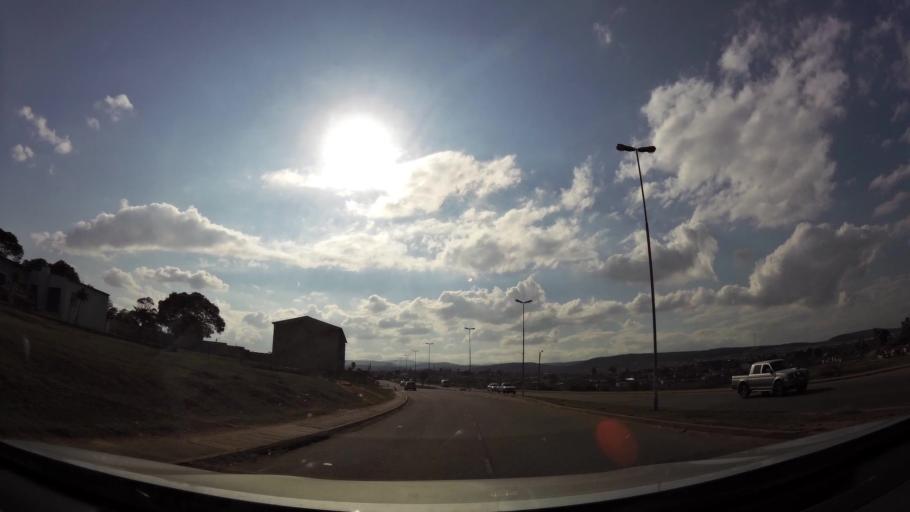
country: ZA
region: Eastern Cape
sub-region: Nelson Mandela Bay Metropolitan Municipality
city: Uitenhage
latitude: -33.7474
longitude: 25.3824
